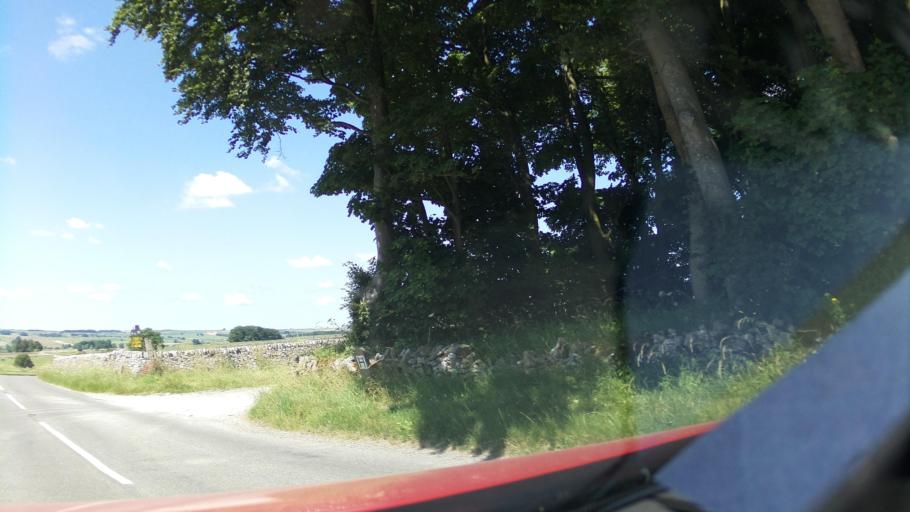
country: GB
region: England
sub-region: Derbyshire
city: Bakewell
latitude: 53.1977
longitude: -1.7404
